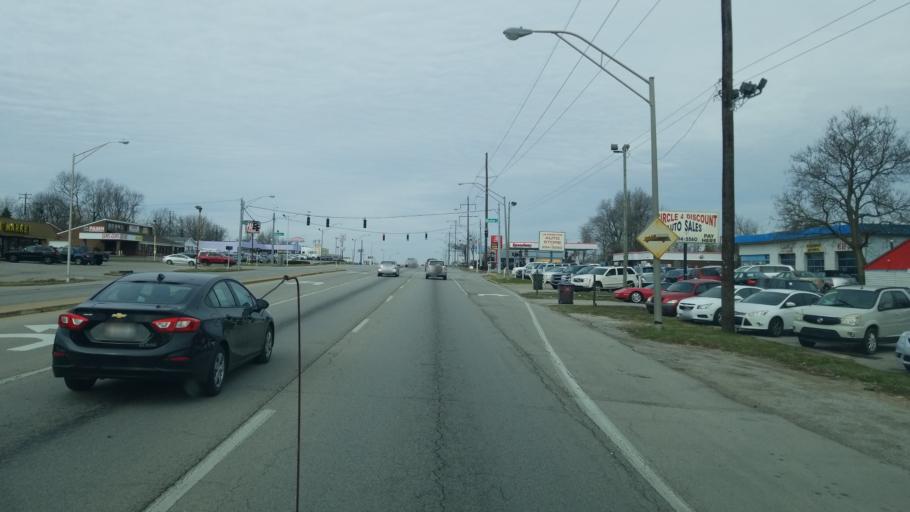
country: US
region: Kentucky
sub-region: Fayette County
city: Lexington-Fayette
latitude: 38.0551
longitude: -84.4599
